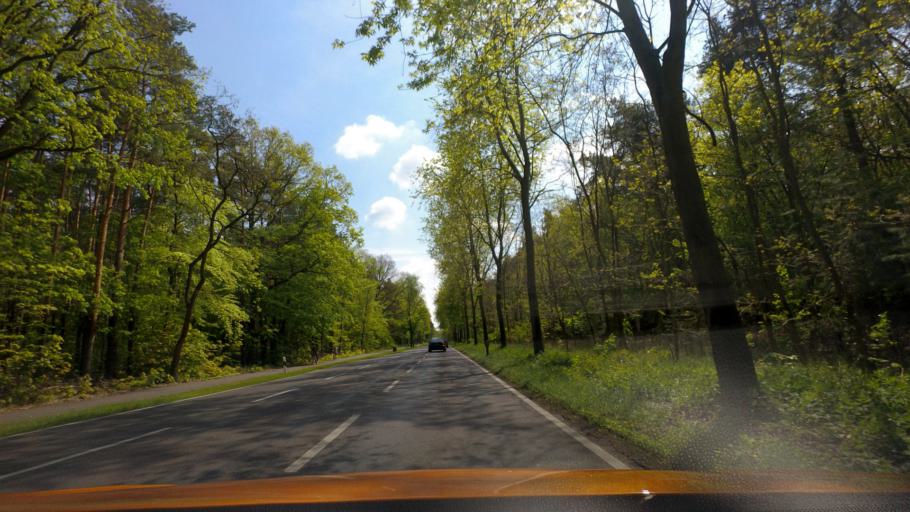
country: DE
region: Berlin
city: Grunau
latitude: 52.4053
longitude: 13.5896
